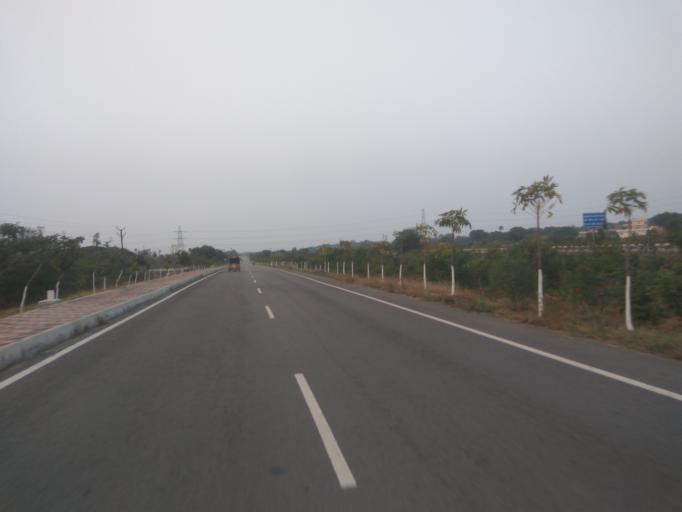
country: IN
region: Telangana
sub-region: Rangareddi
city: Secunderabad
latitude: 17.5457
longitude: 78.6300
